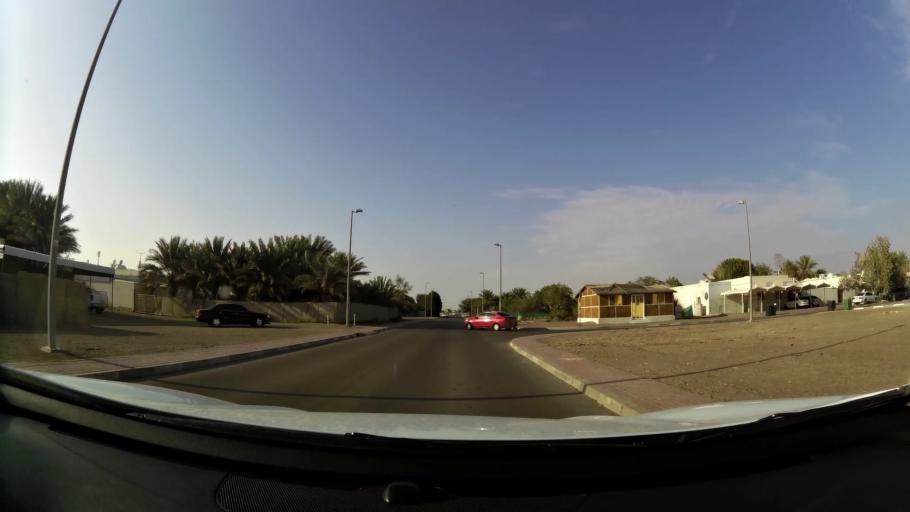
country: AE
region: Abu Dhabi
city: Al Ain
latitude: 24.0844
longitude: 55.8427
